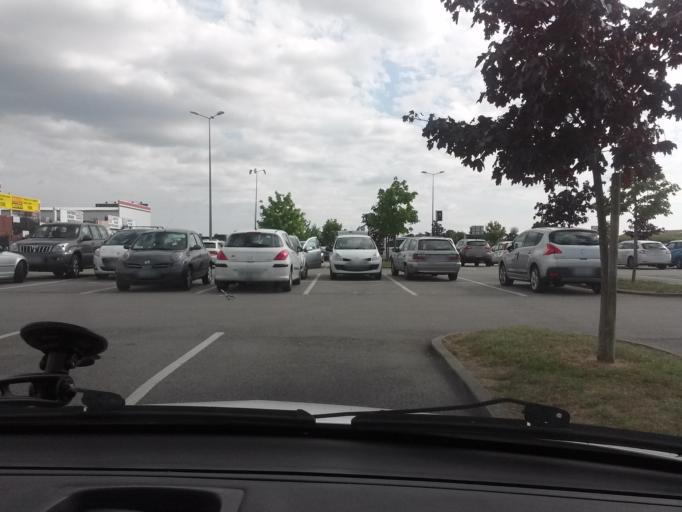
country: FR
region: Pays de la Loire
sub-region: Departement de la Vendee
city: Mouilleron-le-Captif
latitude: 46.7265
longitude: -1.4287
